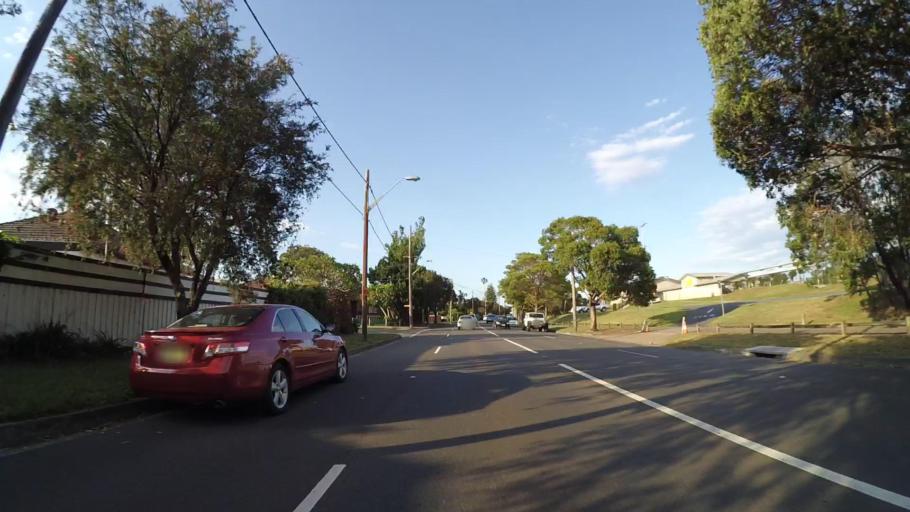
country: AU
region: New South Wales
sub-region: Rockdale
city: Brighton-Le-Sands
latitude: -33.9642
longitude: 151.1430
